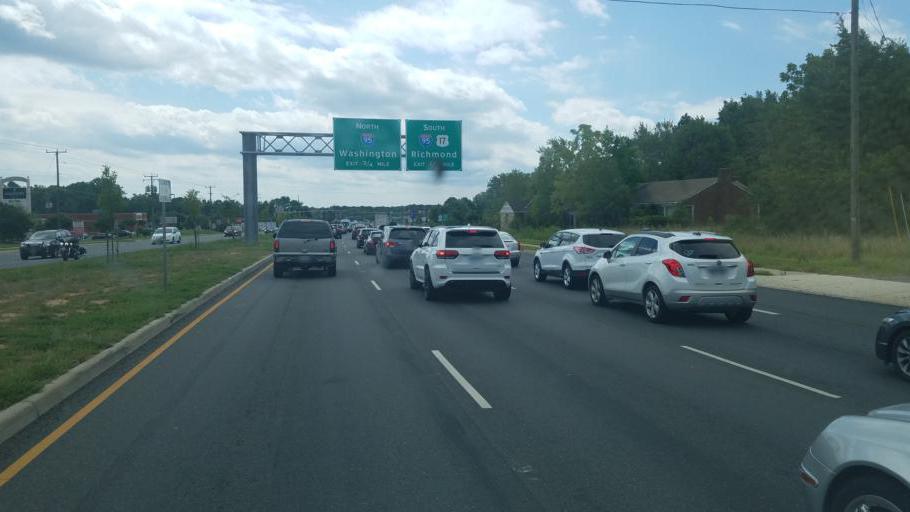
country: US
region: Virginia
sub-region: Stafford County
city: Falmouth
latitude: 38.3493
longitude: -77.5030
